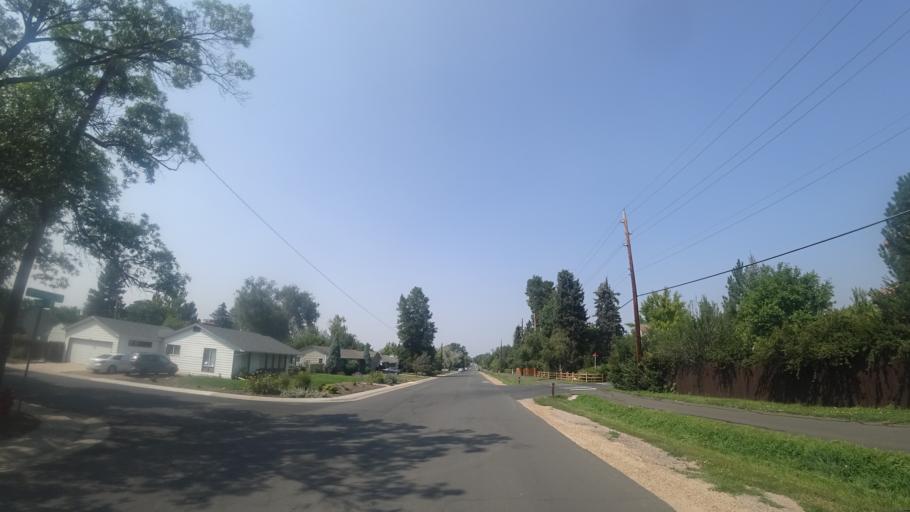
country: US
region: Colorado
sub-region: Arapahoe County
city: Englewood
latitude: 39.6257
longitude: -104.9786
